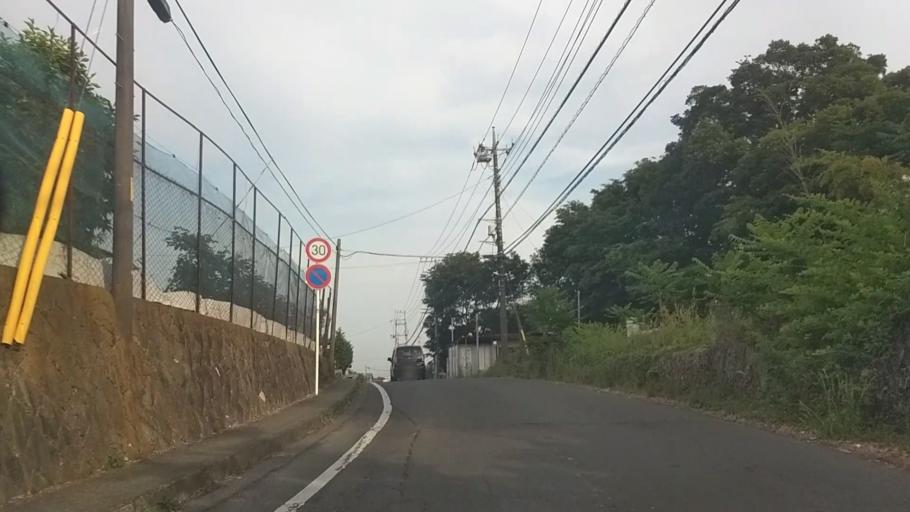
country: JP
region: Kanagawa
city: Odawara
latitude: 35.3232
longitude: 139.1093
